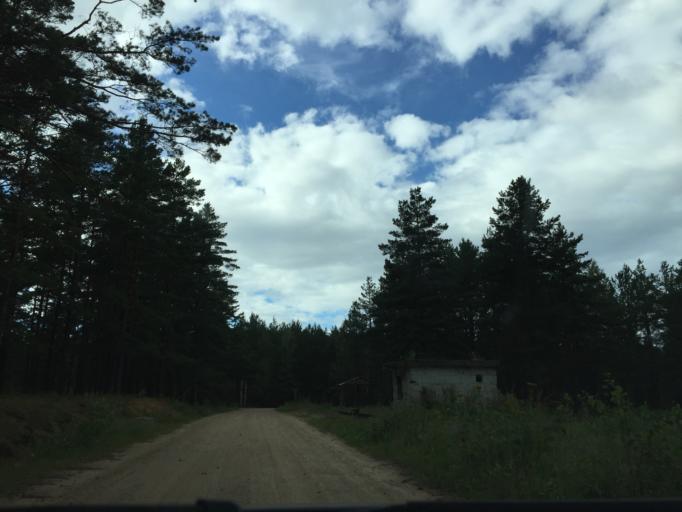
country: LV
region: Saulkrastu
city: Saulkrasti
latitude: 57.1724
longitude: 24.3810
